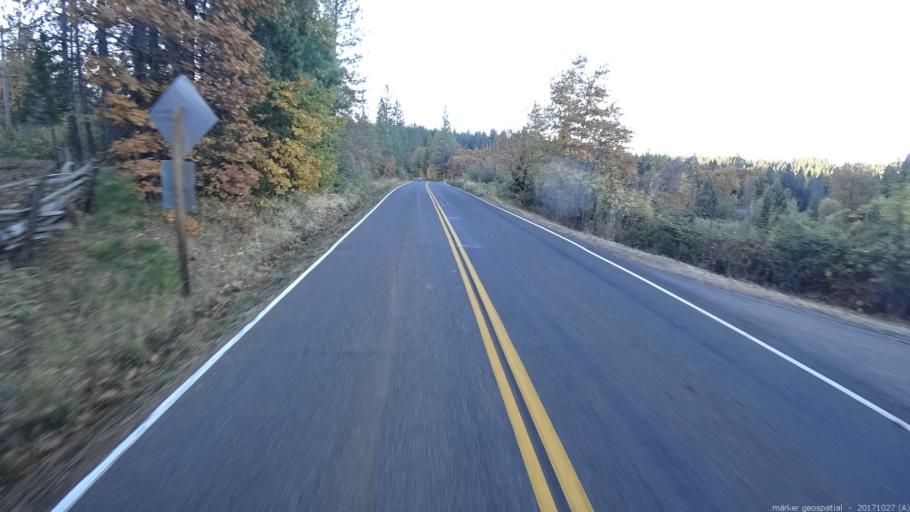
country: US
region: California
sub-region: Shasta County
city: Burney
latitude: 40.9032
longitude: -121.9011
